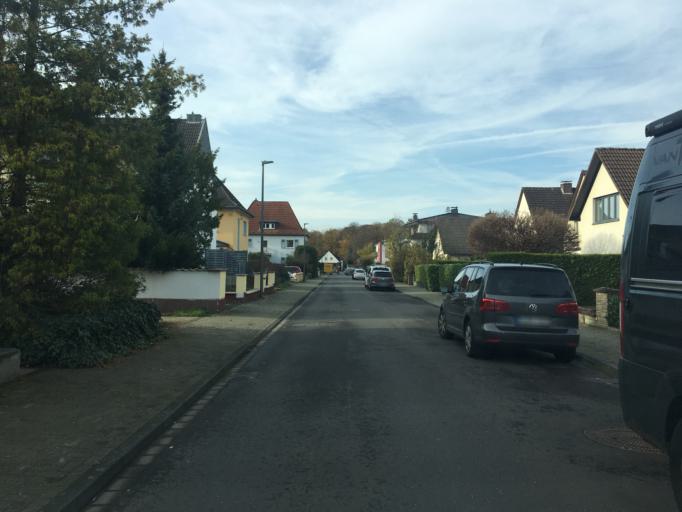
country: DE
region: North Rhine-Westphalia
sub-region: Regierungsbezirk Koln
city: Rath
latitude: 50.9529
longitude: 7.0995
